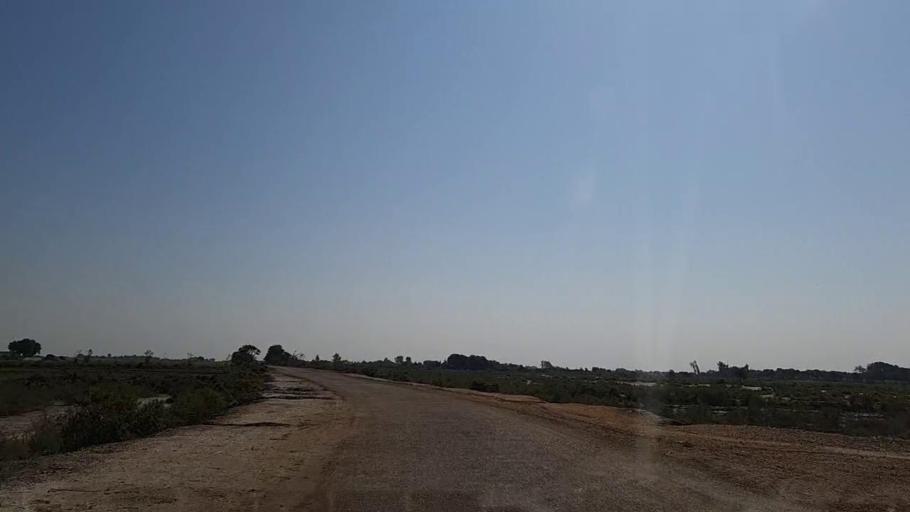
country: PK
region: Sindh
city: Chuhar Jamali
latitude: 24.5263
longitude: 68.0847
